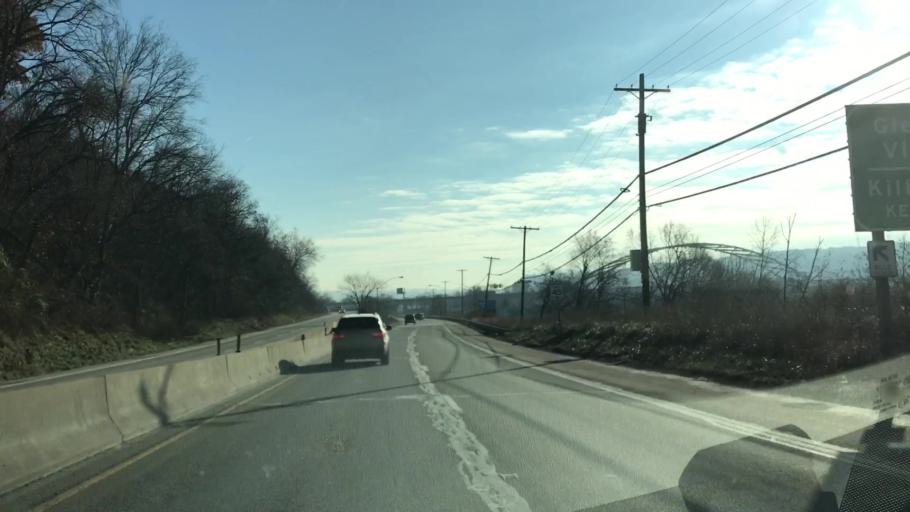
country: US
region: Pennsylvania
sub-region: Allegheny County
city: Coraopolis
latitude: 40.5206
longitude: -80.1405
